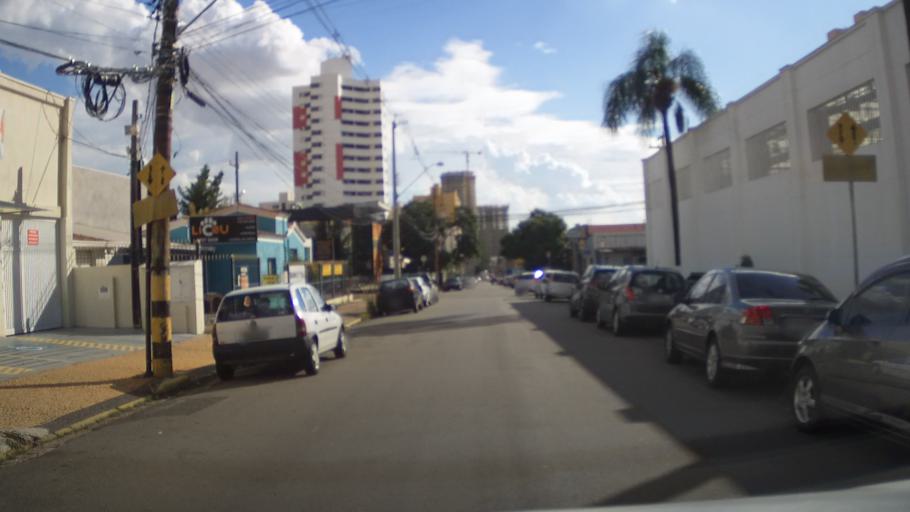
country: BR
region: Sao Paulo
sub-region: Campinas
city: Campinas
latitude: -22.8838
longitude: -47.0598
